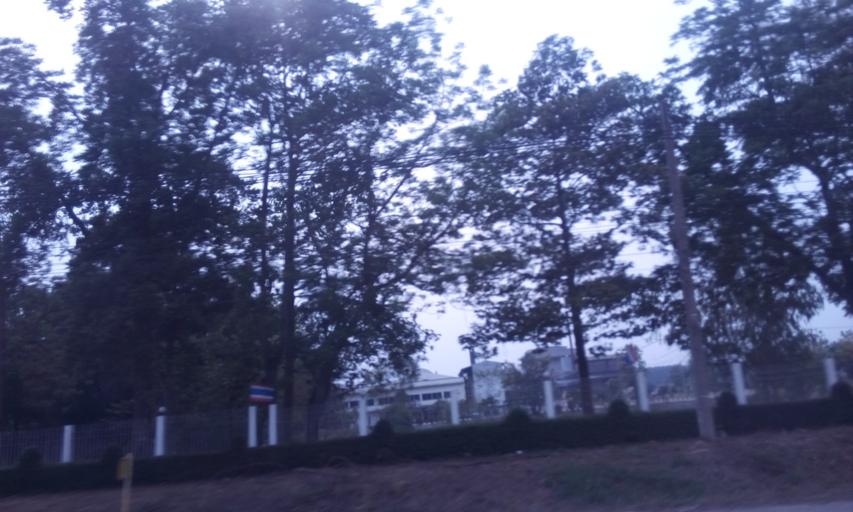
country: TH
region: Chon Buri
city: Ko Chan
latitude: 13.3324
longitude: 101.2703
